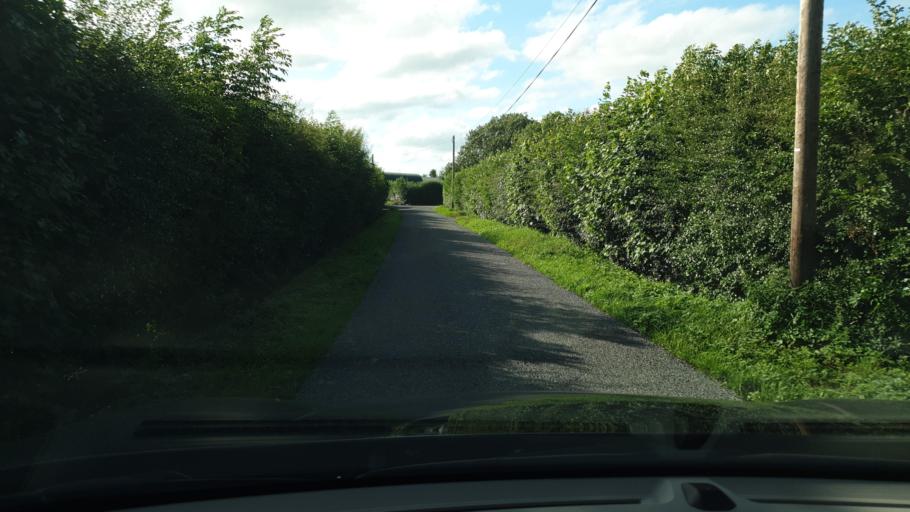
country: IE
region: Leinster
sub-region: An Mhi
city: Ashbourne
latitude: 53.5822
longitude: -6.3515
